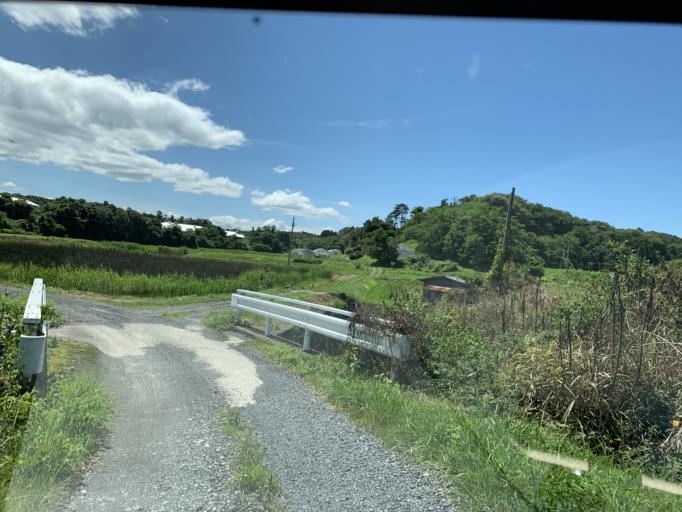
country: JP
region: Iwate
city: Ichinoseki
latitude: 38.9239
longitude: 141.0688
